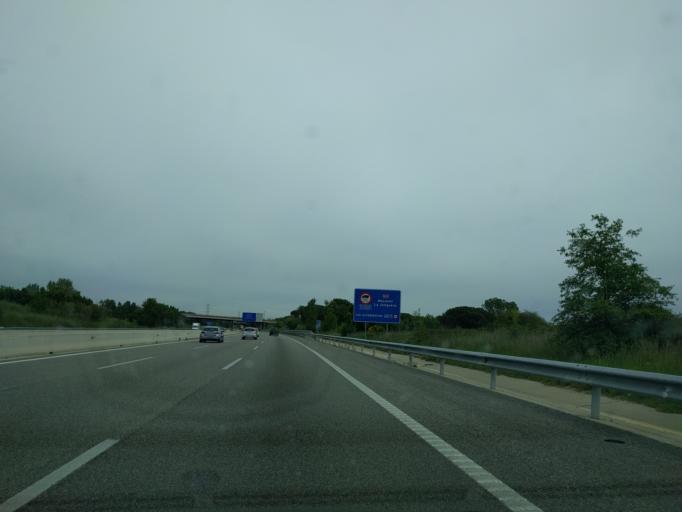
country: ES
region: Catalonia
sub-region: Provincia de Girona
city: Vilobi d'Onyar
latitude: 41.8889
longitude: 2.7742
